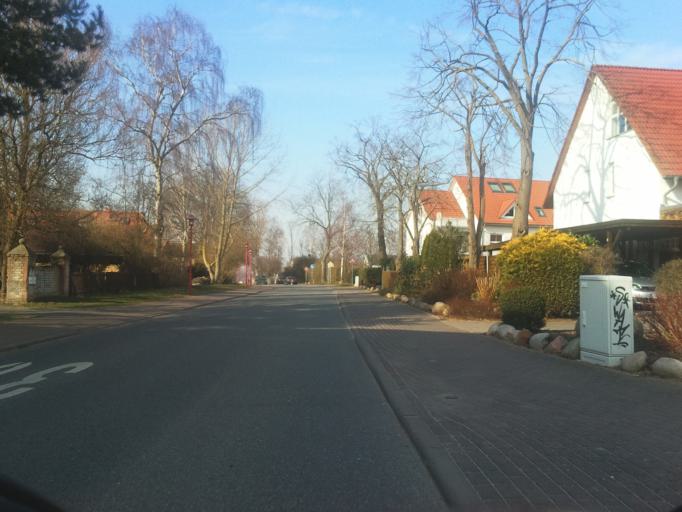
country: DE
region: Mecklenburg-Vorpommern
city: Lambrechtshagen
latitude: 54.1134
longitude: 12.0355
